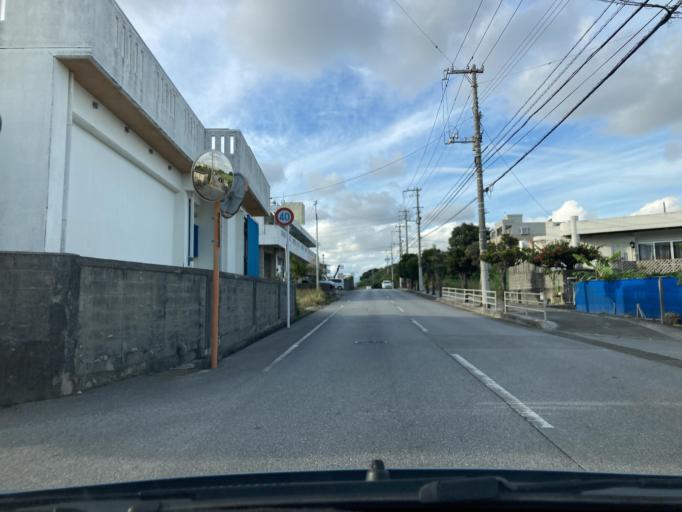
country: JP
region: Okinawa
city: Tomigusuku
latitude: 26.1438
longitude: 127.7335
